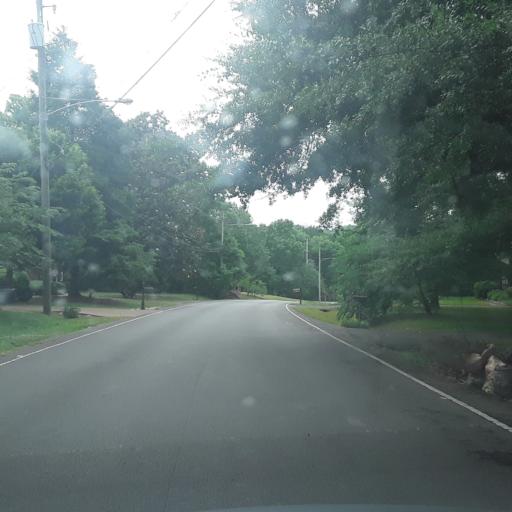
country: US
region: Tennessee
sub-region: Davidson County
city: Oak Hill
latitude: 36.0694
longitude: -86.7576
